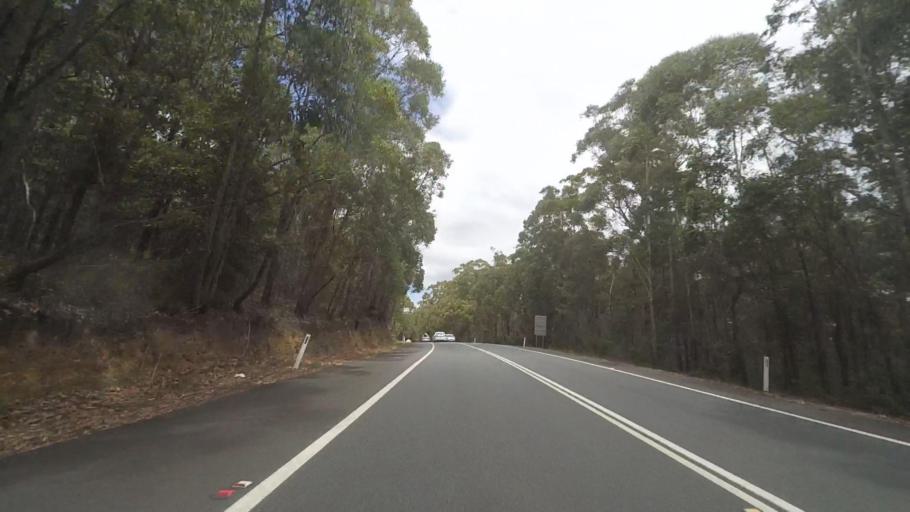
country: AU
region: New South Wales
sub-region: Shoalhaven Shire
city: Milton
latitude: -35.1542
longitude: 150.4510
